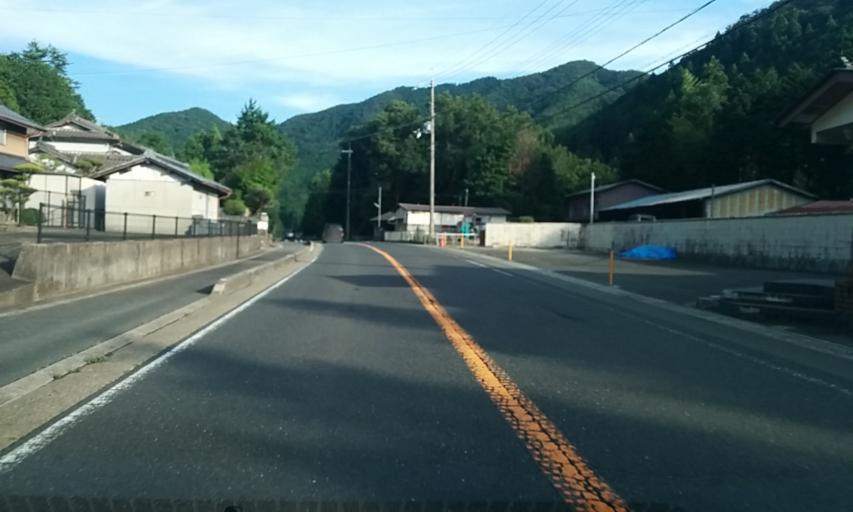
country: JP
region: Kyoto
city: Ayabe
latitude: 35.2485
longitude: 135.2800
